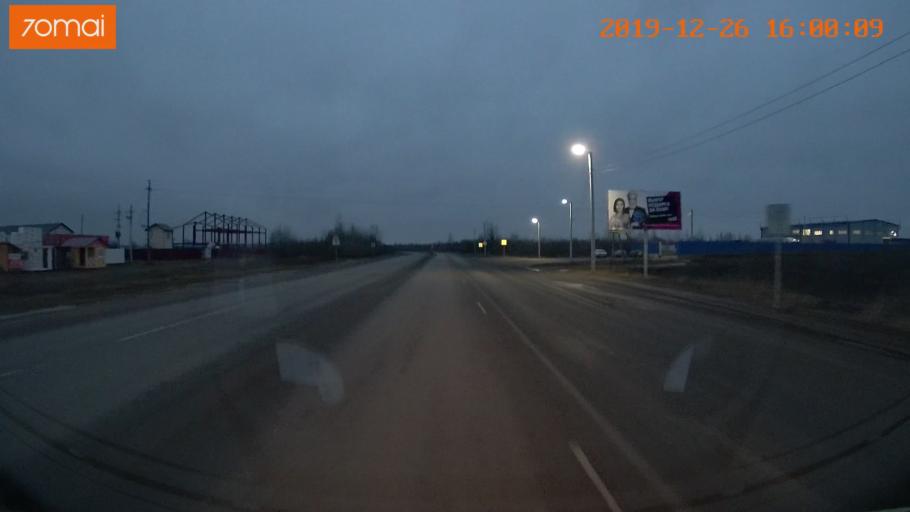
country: RU
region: Jaroslavl
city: Rybinsk
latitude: 58.0271
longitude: 38.8033
